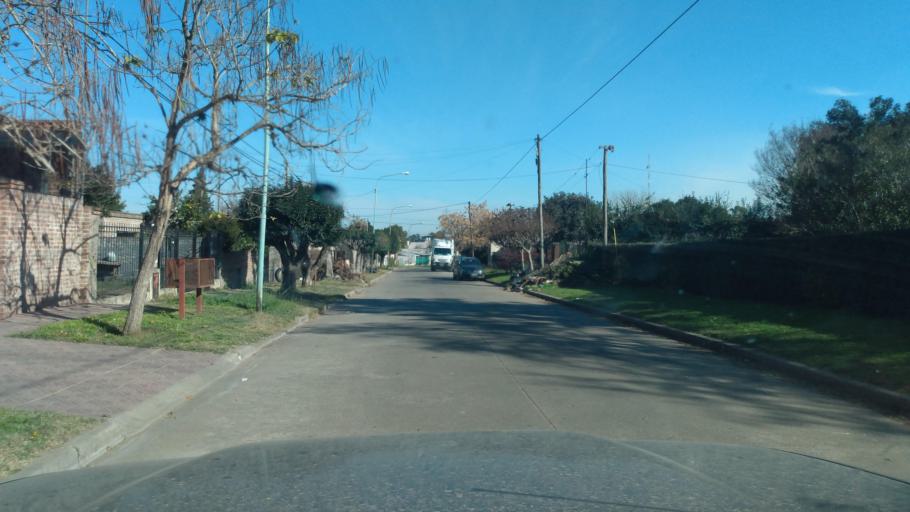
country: AR
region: Buenos Aires
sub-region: Partido de Lujan
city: Lujan
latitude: -34.5837
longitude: -59.1093
